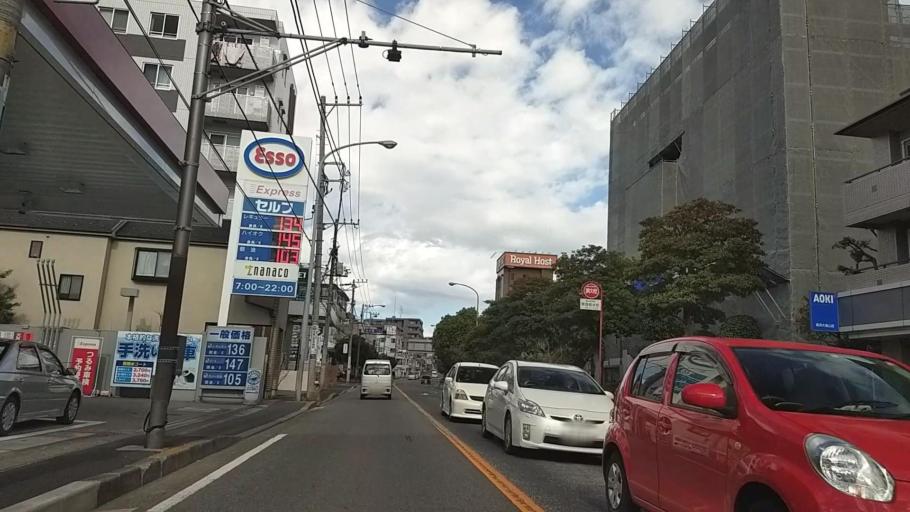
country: JP
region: Kanagawa
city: Yokohama
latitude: 35.5186
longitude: 139.6323
